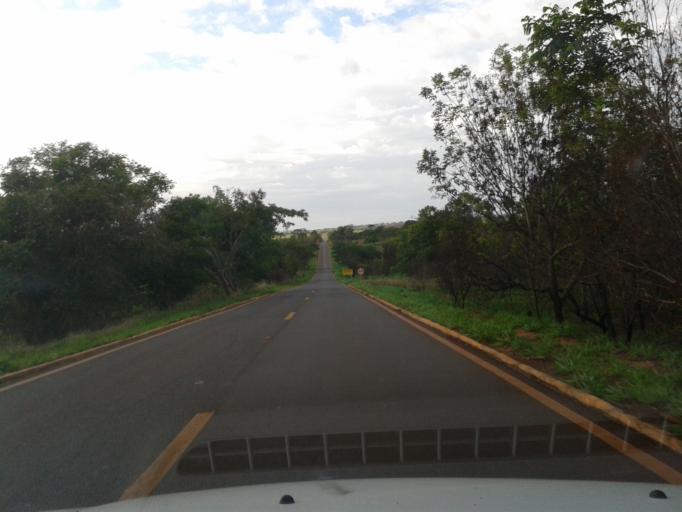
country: BR
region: Minas Gerais
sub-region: Ituiutaba
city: Ituiutaba
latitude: -19.0739
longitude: -49.7660
